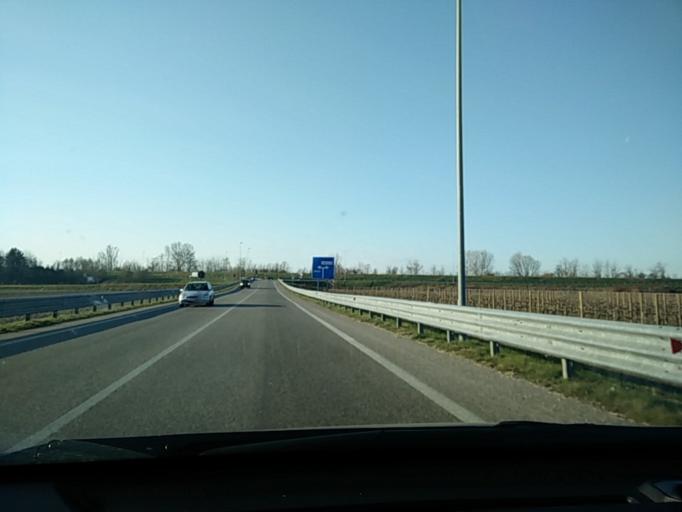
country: IT
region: Veneto
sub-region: Provincia di Venezia
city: Passarella
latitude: 45.6107
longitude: 12.5938
